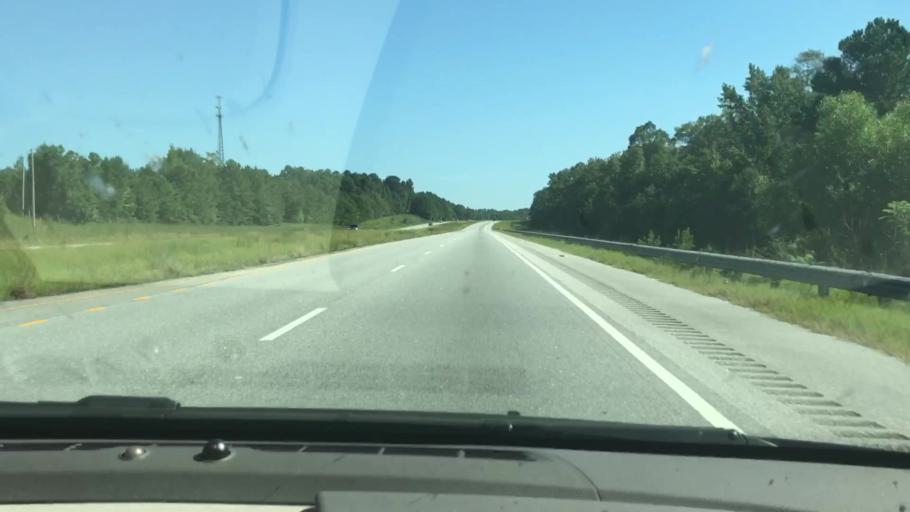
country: US
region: Alabama
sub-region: Russell County
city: Ladonia
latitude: 32.3852
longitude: -85.0800
